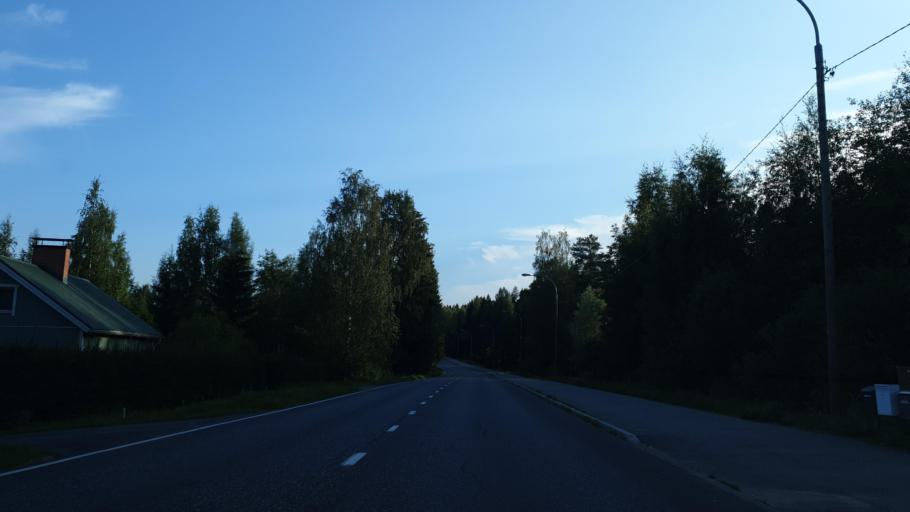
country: FI
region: Northern Savo
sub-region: Koillis-Savo
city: Kaavi
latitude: 62.9811
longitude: 28.4984
